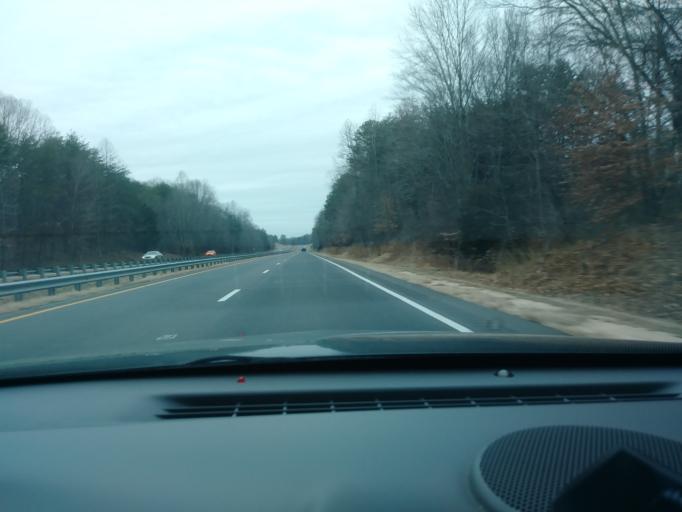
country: US
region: North Carolina
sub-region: Forsyth County
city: Lewisville
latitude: 36.0982
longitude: -80.4585
